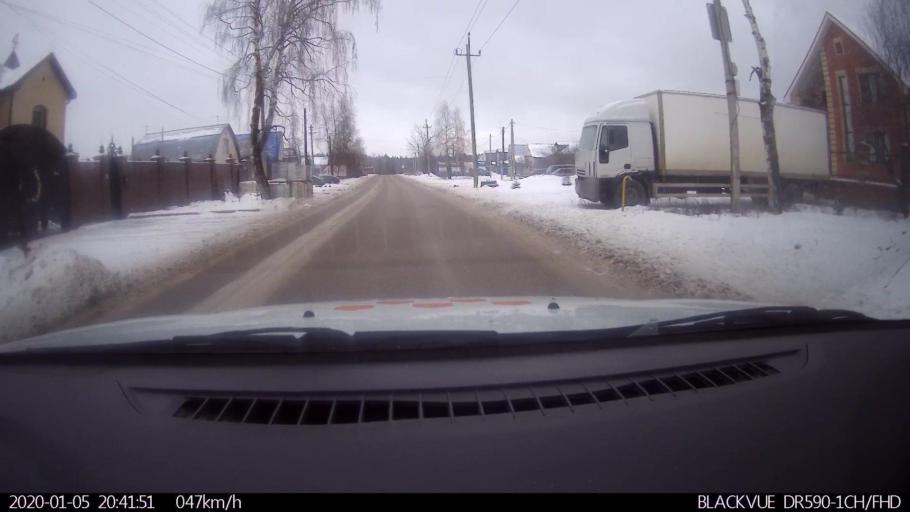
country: RU
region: Nizjnij Novgorod
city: Lukino
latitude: 56.4002
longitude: 43.7295
